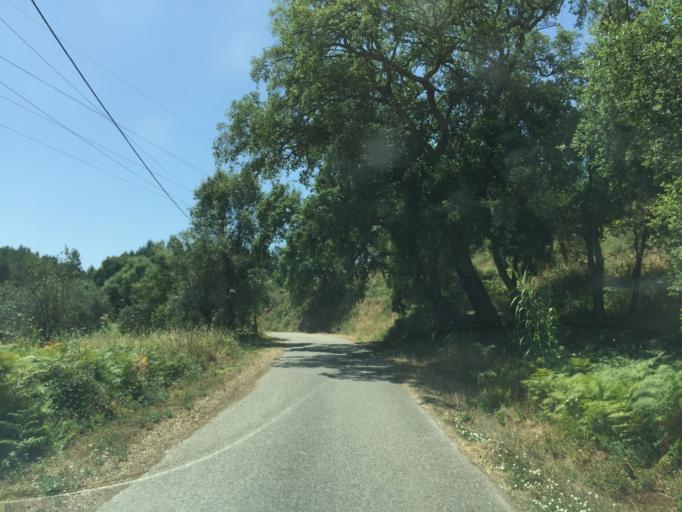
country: PT
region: Santarem
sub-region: Ferreira do Zezere
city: Ferreira do Zezere
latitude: 39.6527
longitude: -8.3025
